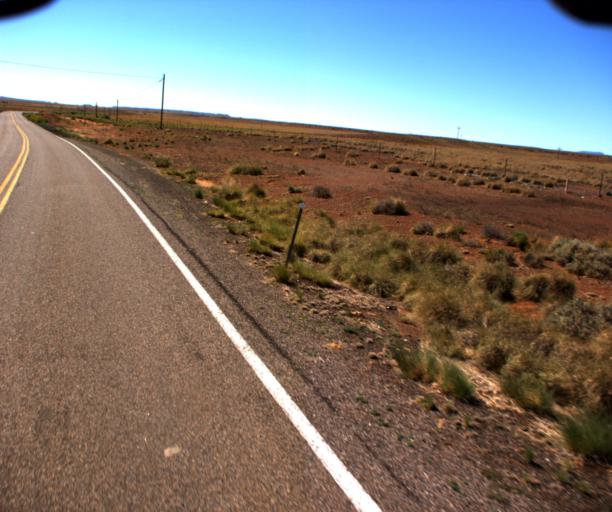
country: US
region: Arizona
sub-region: Coconino County
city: LeChee
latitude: 35.1550
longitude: -110.9034
